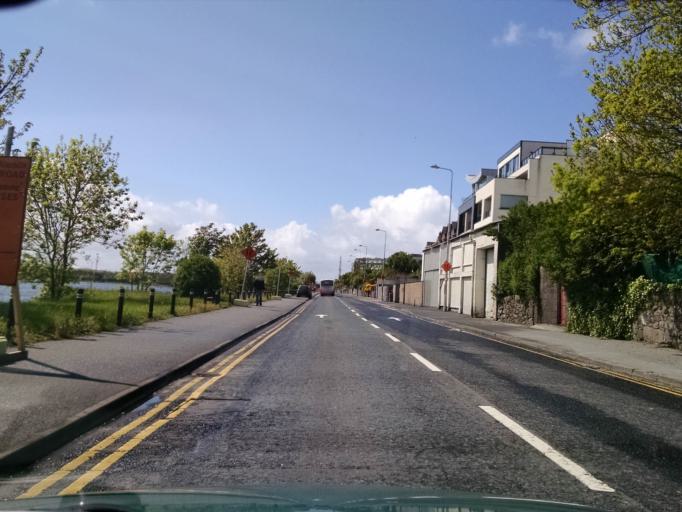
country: IE
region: Connaught
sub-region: County Galway
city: Gaillimh
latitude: 53.2774
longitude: -9.0387
